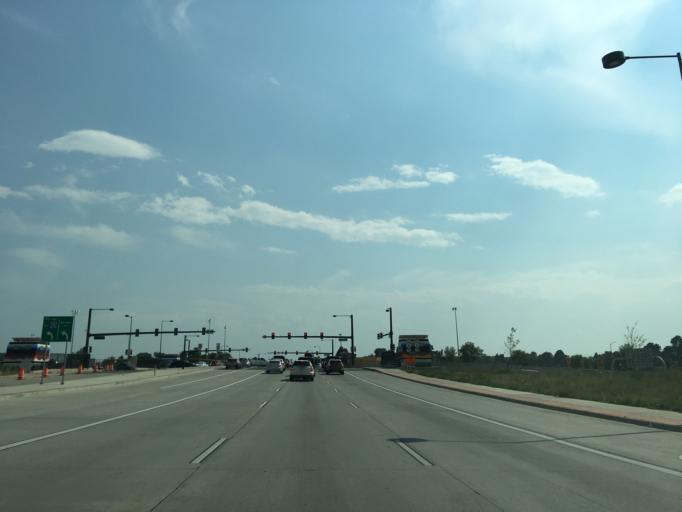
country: US
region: Colorado
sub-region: Denver County
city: Denver
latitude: 39.7269
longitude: -105.0252
